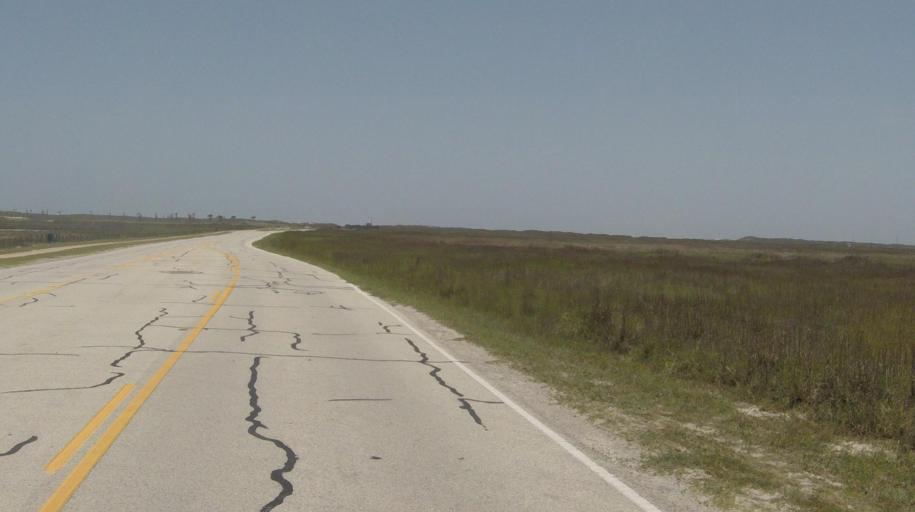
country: US
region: Texas
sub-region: San Patricio County
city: Ingleside
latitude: 27.6207
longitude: -97.2085
